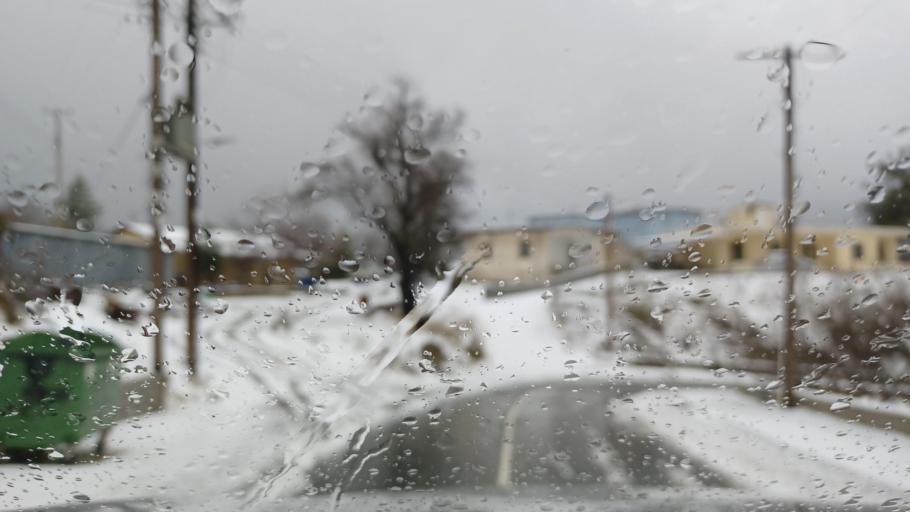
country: CY
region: Limassol
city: Pelendri
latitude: 34.9028
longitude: 32.9644
